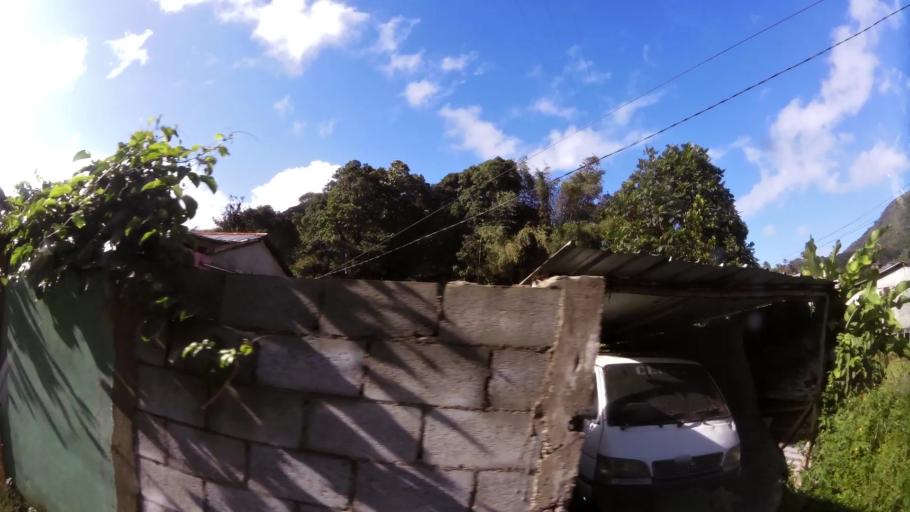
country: DM
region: Saint John
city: Portsmouth
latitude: 15.5850
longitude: -61.4117
